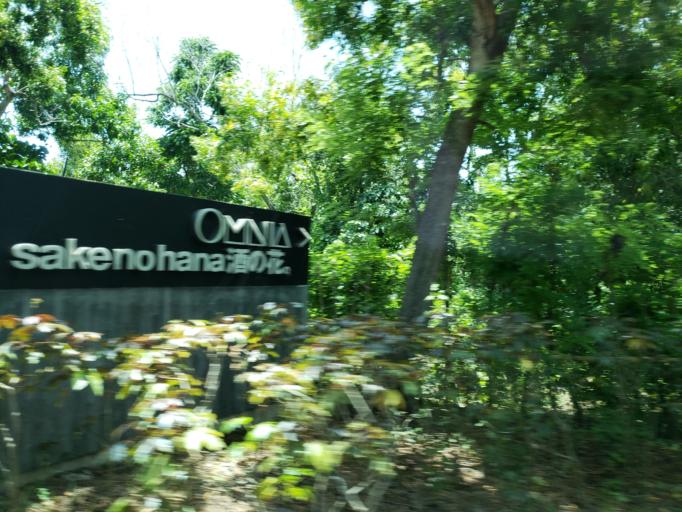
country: ID
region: Bali
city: Kangin
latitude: -8.8444
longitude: 115.1401
